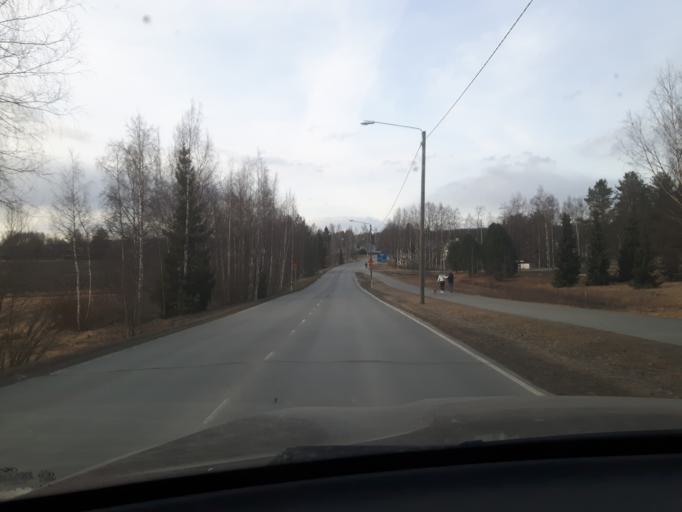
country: FI
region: Pirkanmaa
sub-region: Tampere
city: Kangasala
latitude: 61.4587
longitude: 24.0352
